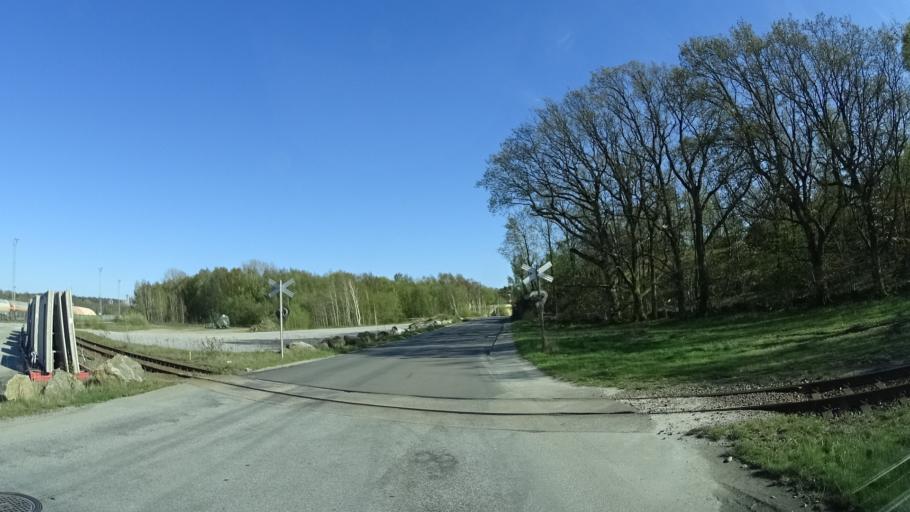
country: SE
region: Vaestra Goetaland
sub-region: Stenungsunds Kommun
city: Stenungsund
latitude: 58.0821
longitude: 11.8214
